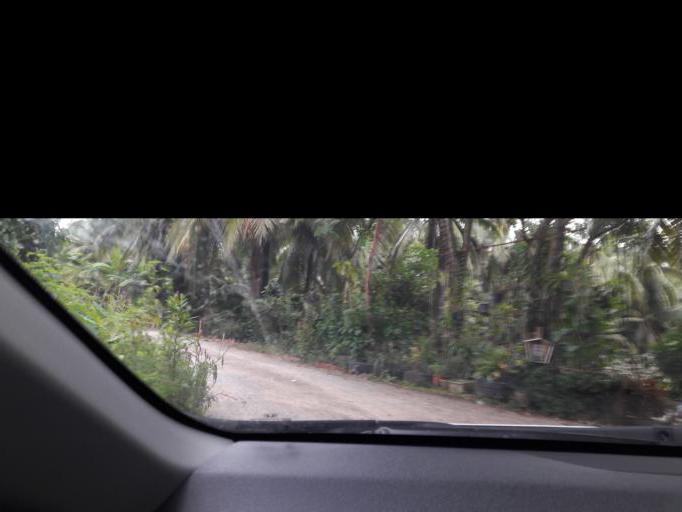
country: TH
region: Ratchaburi
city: Damnoen Saduak
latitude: 13.5478
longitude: 99.9758
